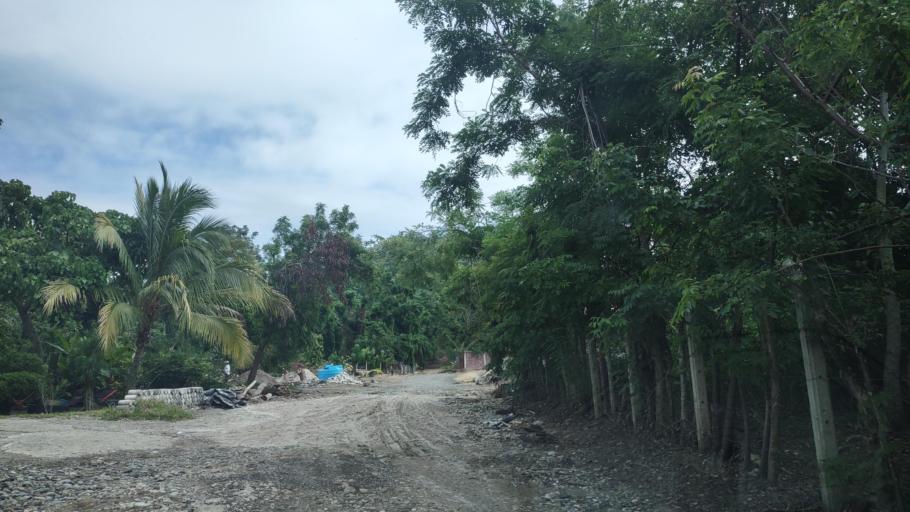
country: MX
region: Veracruz
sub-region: Papantla
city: Residencial Tajin
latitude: 20.5931
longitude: -97.4178
